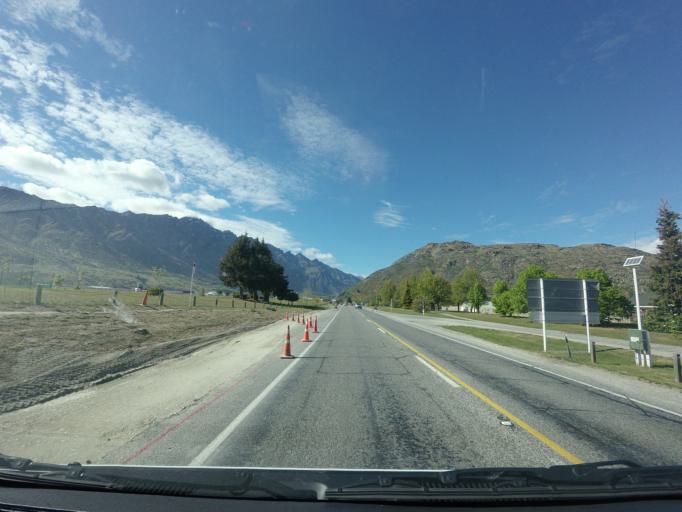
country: NZ
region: Otago
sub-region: Queenstown-Lakes District
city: Queenstown
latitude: -45.0179
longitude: 168.7325
